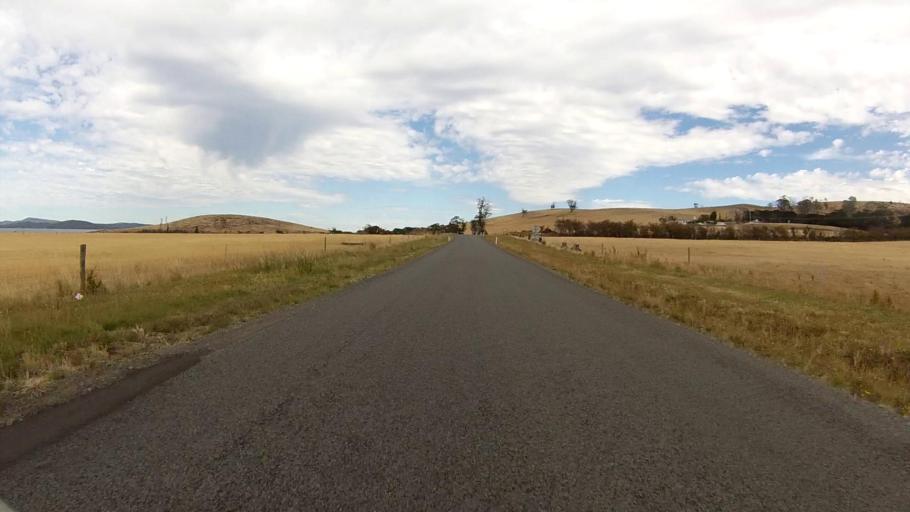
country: AU
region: Tasmania
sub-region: Sorell
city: Sorell
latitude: -42.8945
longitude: 147.7774
